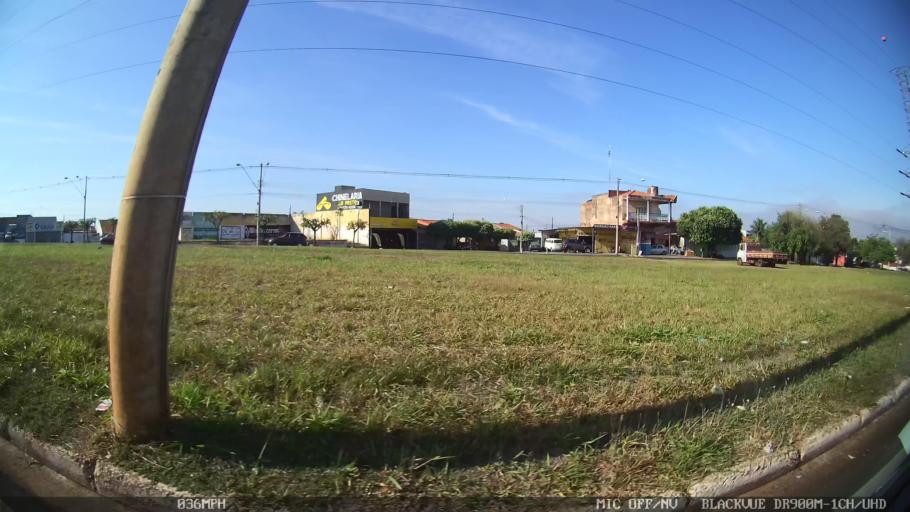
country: BR
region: Sao Paulo
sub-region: Sao Jose Do Rio Preto
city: Sao Jose do Rio Preto
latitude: -20.7734
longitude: -49.3952
